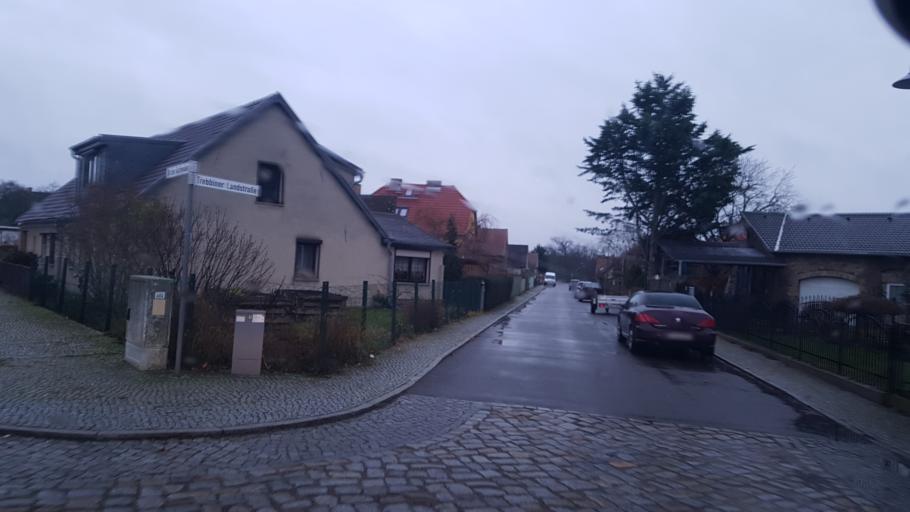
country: DE
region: Brandenburg
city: Ludwigsfelde
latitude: 52.3134
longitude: 13.2045
